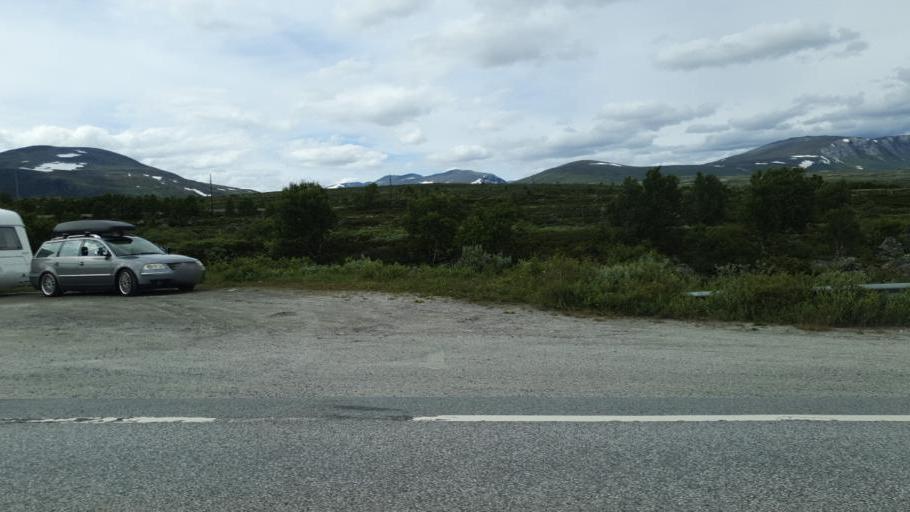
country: NO
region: Sor-Trondelag
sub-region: Oppdal
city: Oppdal
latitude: 62.2675
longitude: 9.5819
